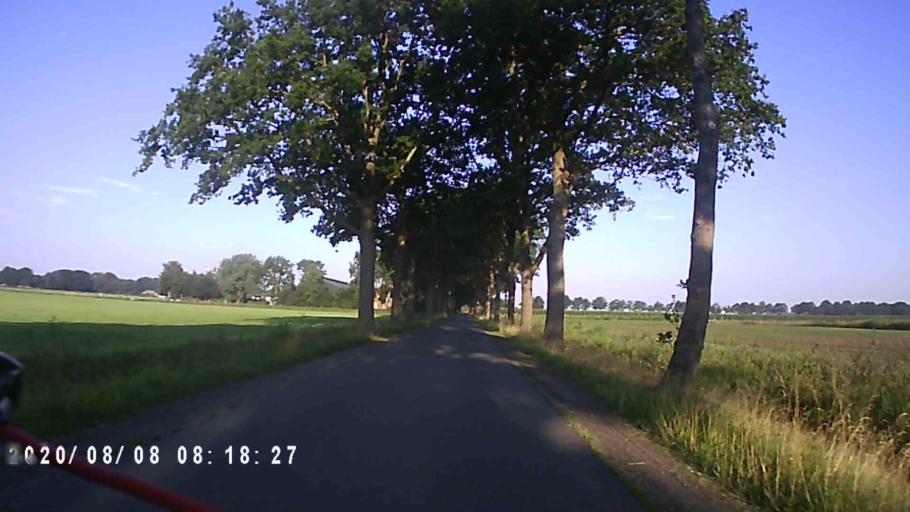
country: NL
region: Groningen
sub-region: Gemeente Leek
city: Leek
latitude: 53.0963
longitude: 6.3232
